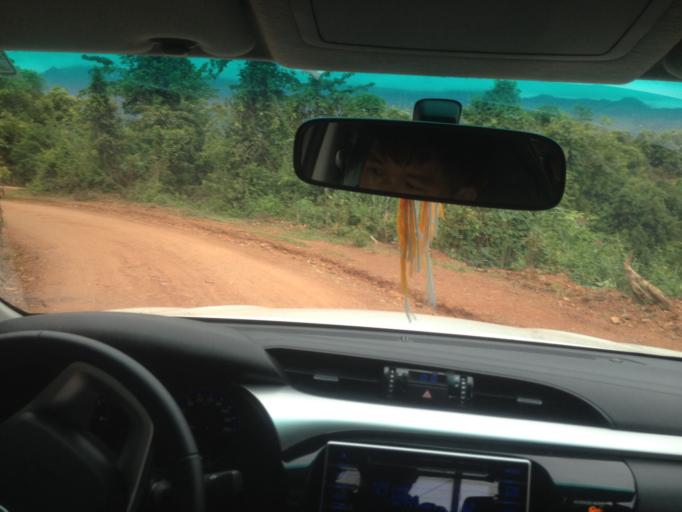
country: TH
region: Nan
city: Chaloem Phra Kiat
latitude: 19.9674
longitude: 101.1380
